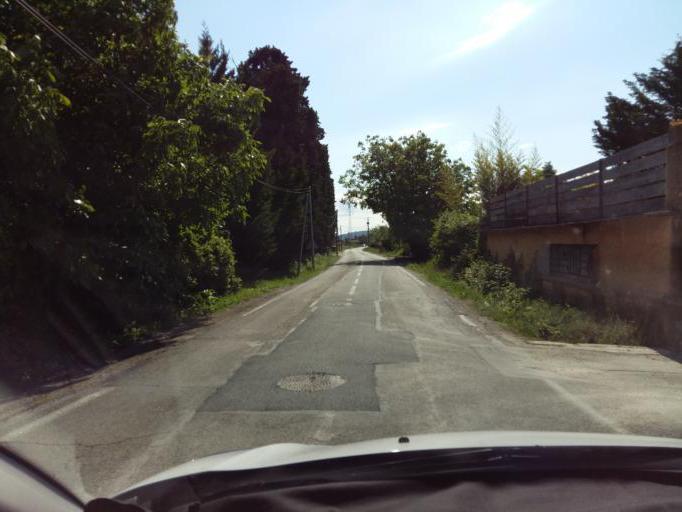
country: FR
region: Provence-Alpes-Cote d'Azur
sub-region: Departement du Vaucluse
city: Robion
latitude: 43.8585
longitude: 5.0918
